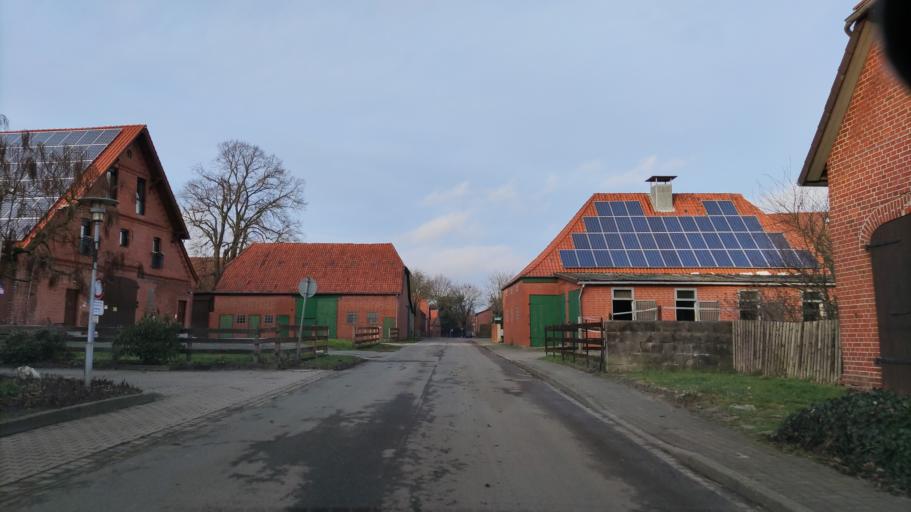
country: DE
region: Lower Saxony
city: Echem
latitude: 53.3366
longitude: 10.5302
